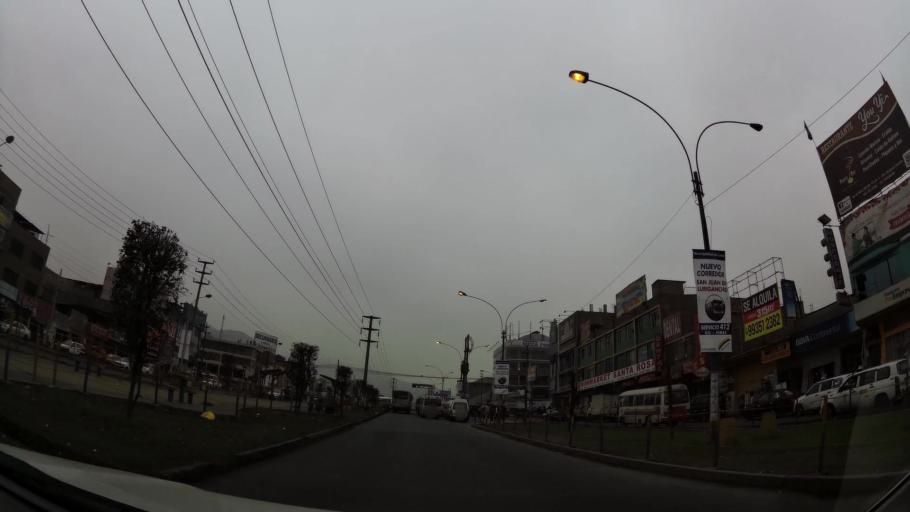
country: PE
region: Lima
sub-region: Lima
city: Independencia
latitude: -11.9483
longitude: -76.9854
